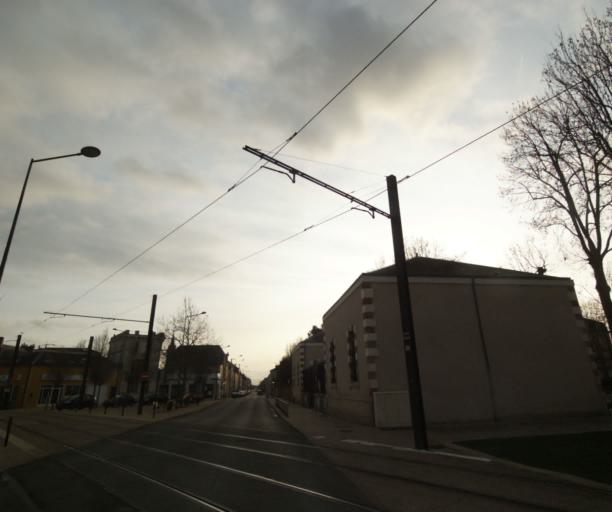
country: FR
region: Pays de la Loire
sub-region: Departement de la Sarthe
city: Le Mans
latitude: 48.0111
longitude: 0.1817
